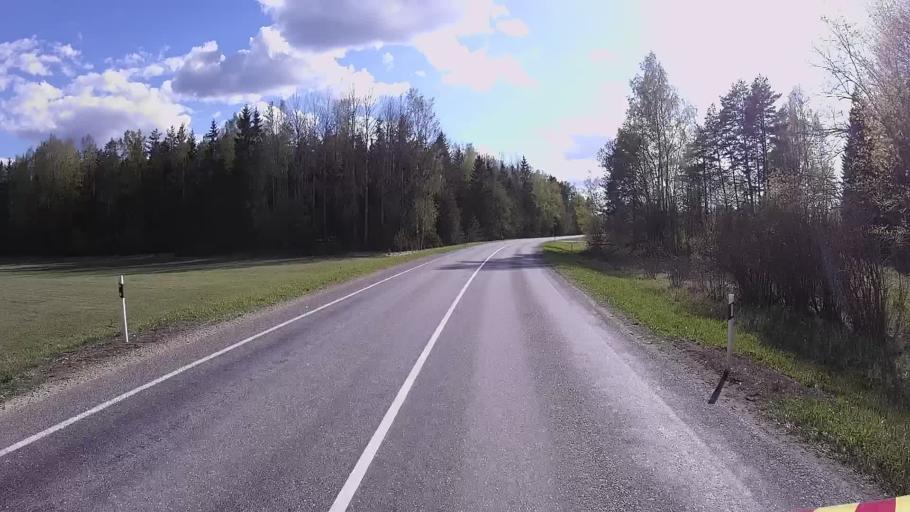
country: EE
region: Jogevamaa
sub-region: Jogeva linn
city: Jogeva
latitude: 58.7390
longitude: 26.2985
